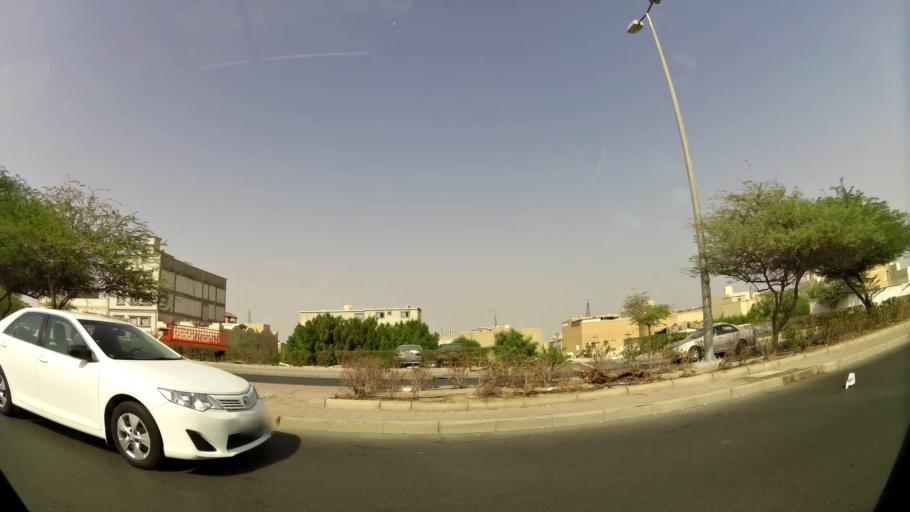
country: KW
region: Muhafazat al Jahra'
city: Al Jahra'
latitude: 29.3201
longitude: 47.6565
